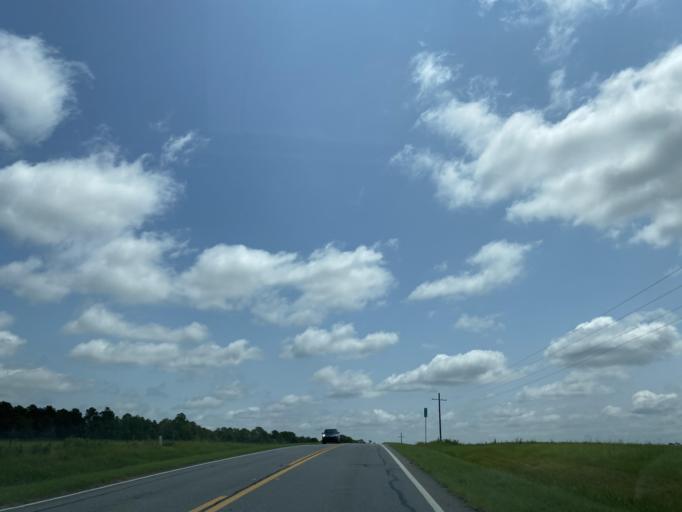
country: US
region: Georgia
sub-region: Telfair County
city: Helena
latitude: 32.0148
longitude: -83.0852
